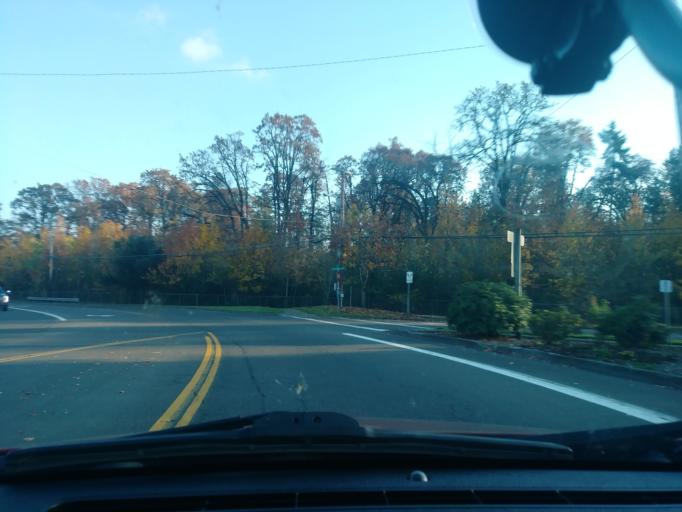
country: US
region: Oregon
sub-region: Washington County
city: Forest Grove
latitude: 45.5201
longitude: -123.1214
